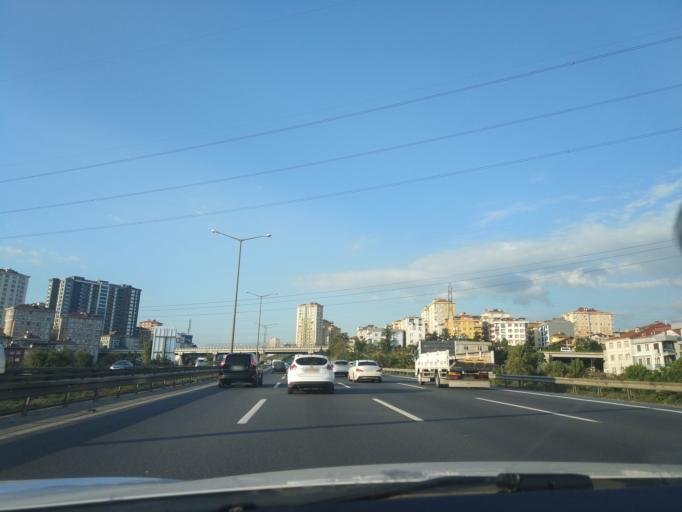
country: TR
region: Istanbul
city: Umraniye
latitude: 41.0074
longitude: 29.1218
